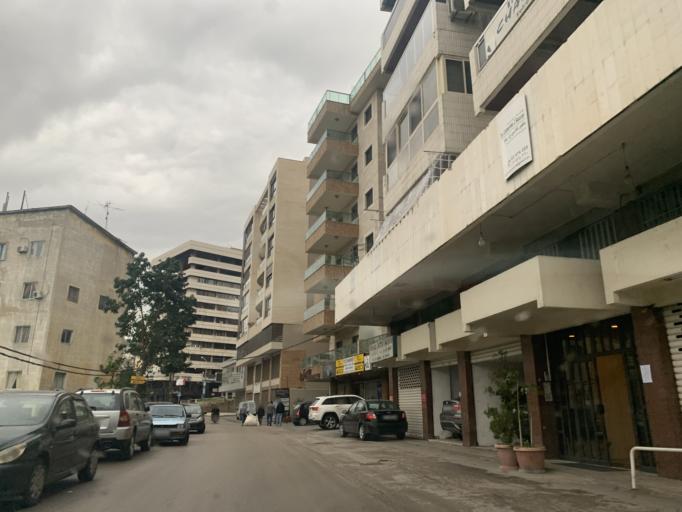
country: LB
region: Mont-Liban
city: Djounie
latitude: 33.9819
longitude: 35.6259
